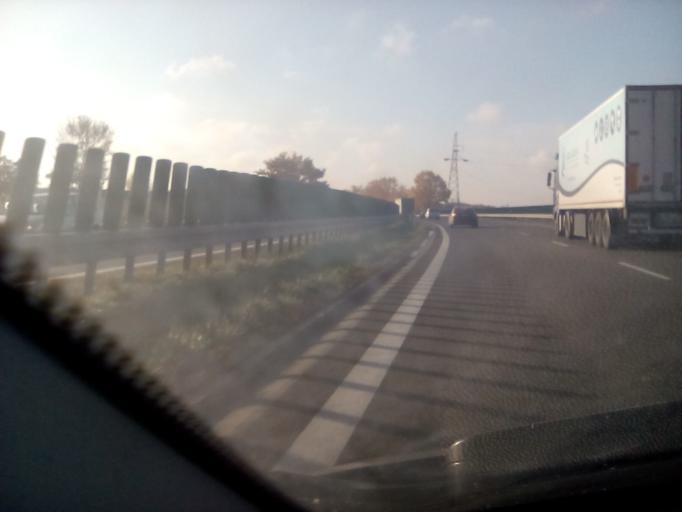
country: PL
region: Masovian Voivodeship
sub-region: Powiat grojecki
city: Grojec
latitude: 51.8906
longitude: 20.8567
